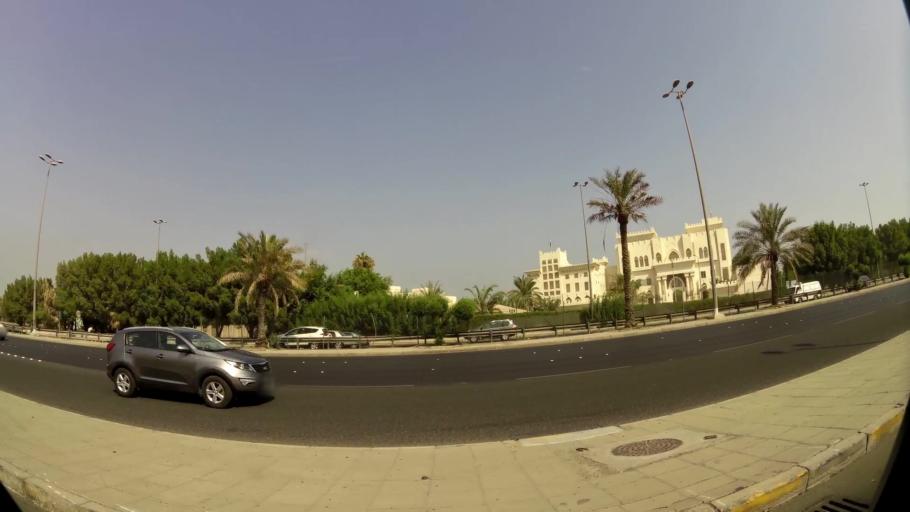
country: KW
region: Al Asimah
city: Ad Dasmah
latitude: 29.3634
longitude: 48.0143
